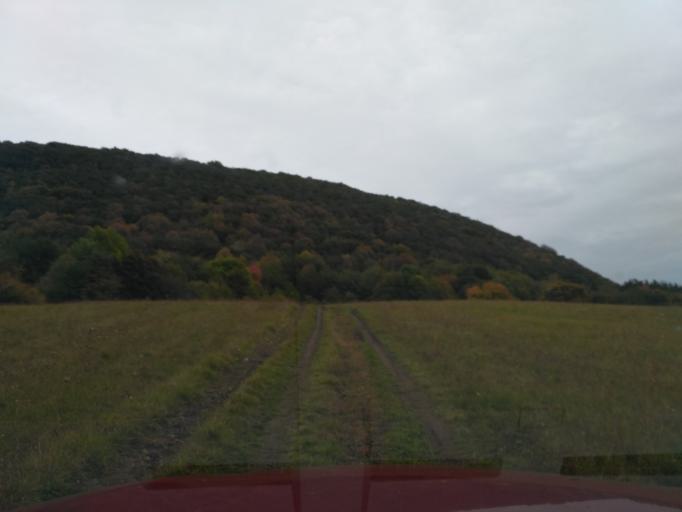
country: SK
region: Presovsky
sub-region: Okres Presov
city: Presov
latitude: 48.8953
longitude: 21.3382
